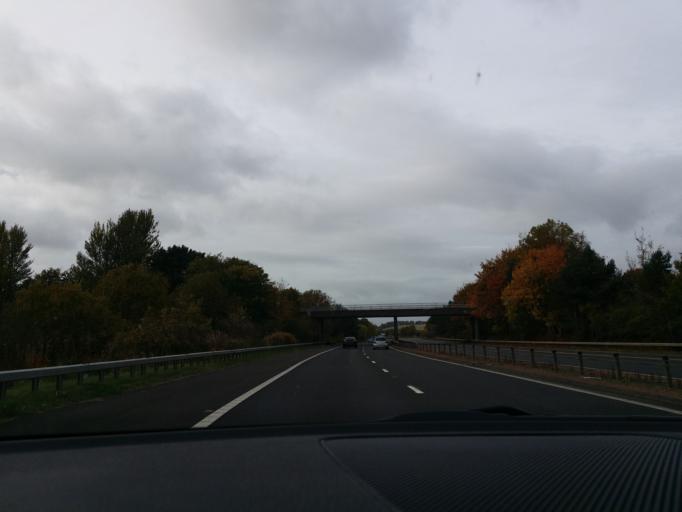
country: GB
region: Scotland
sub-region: West Lothian
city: Linlithgow
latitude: 55.9818
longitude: -3.6227
